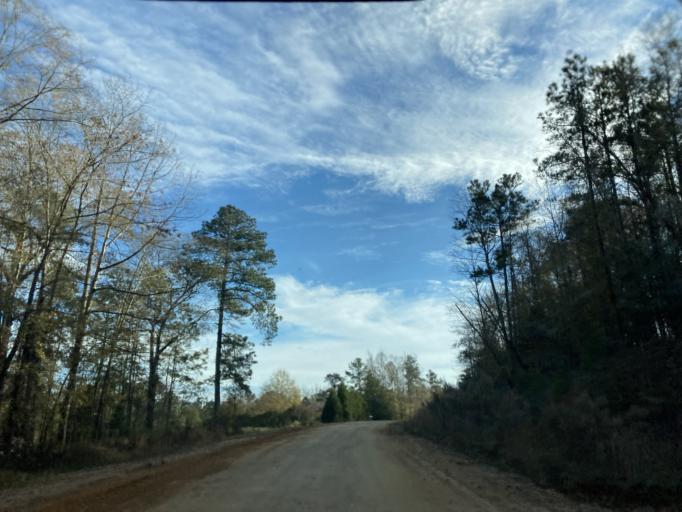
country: US
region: Georgia
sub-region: Jones County
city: Gray
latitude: 32.9054
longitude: -83.4906
